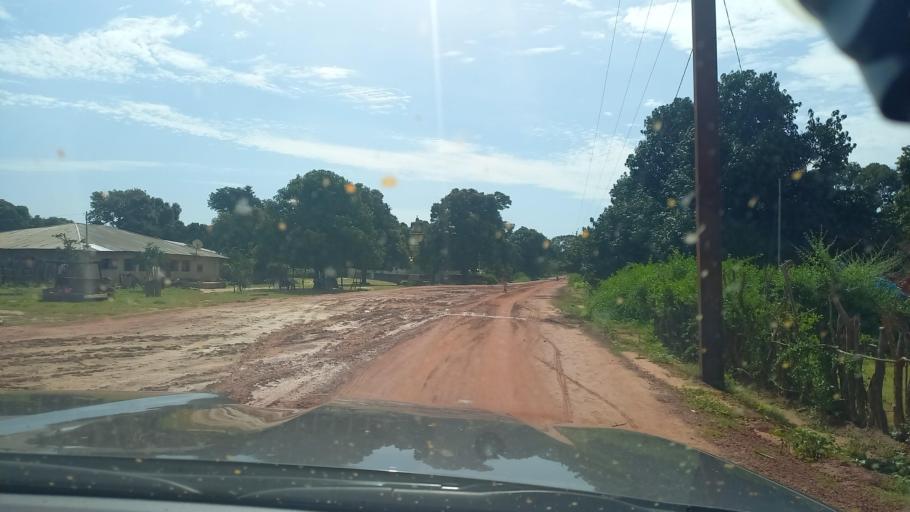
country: SN
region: Ziguinchor
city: Ziguinchor
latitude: 12.6747
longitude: -16.1940
